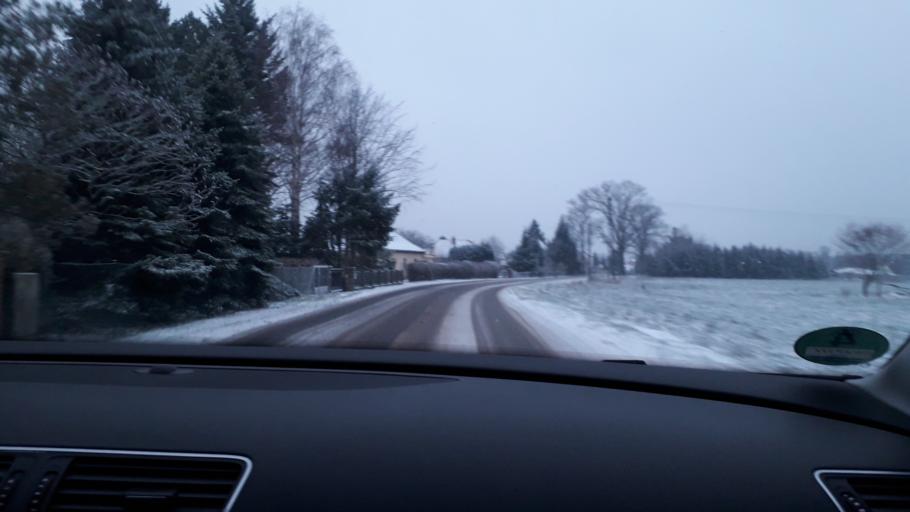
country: DE
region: Brandenburg
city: Spremberg
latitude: 51.5837
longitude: 14.4189
